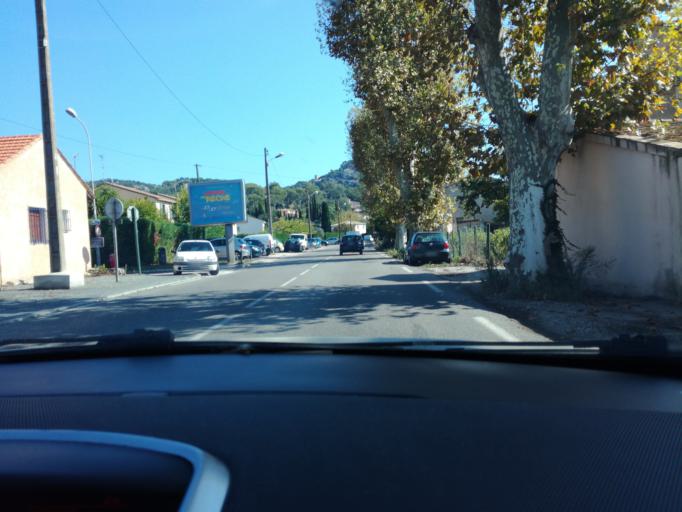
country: FR
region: Provence-Alpes-Cote d'Azur
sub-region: Departement du Var
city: Hyeres
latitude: 43.1257
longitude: 6.1114
